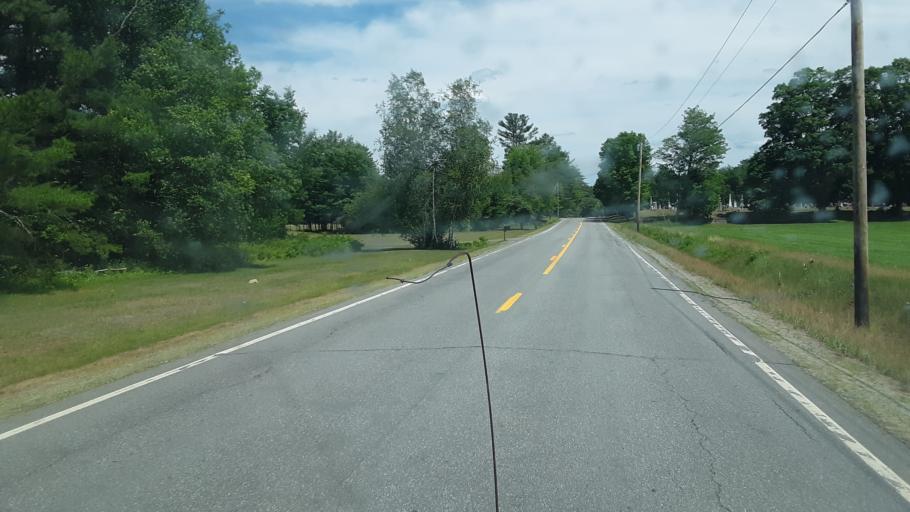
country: US
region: Maine
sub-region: Franklin County
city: Chesterville
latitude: 44.5934
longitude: -70.1259
